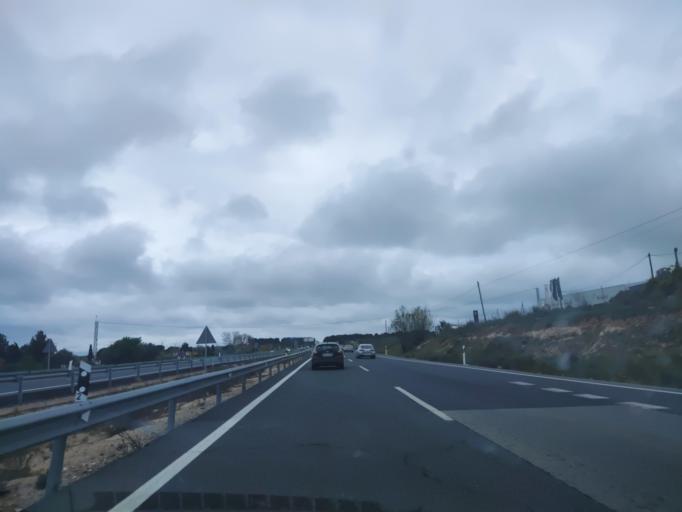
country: ES
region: Castille-La Mancha
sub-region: Province of Toledo
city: Yuncos
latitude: 40.0697
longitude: -3.8940
